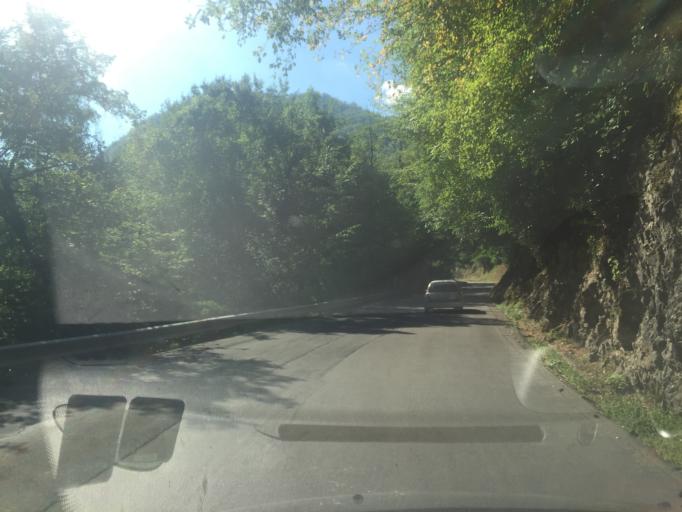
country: IT
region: Tuscany
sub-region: Provincia di Lucca
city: Careggine
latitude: 44.1327
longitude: 10.3064
